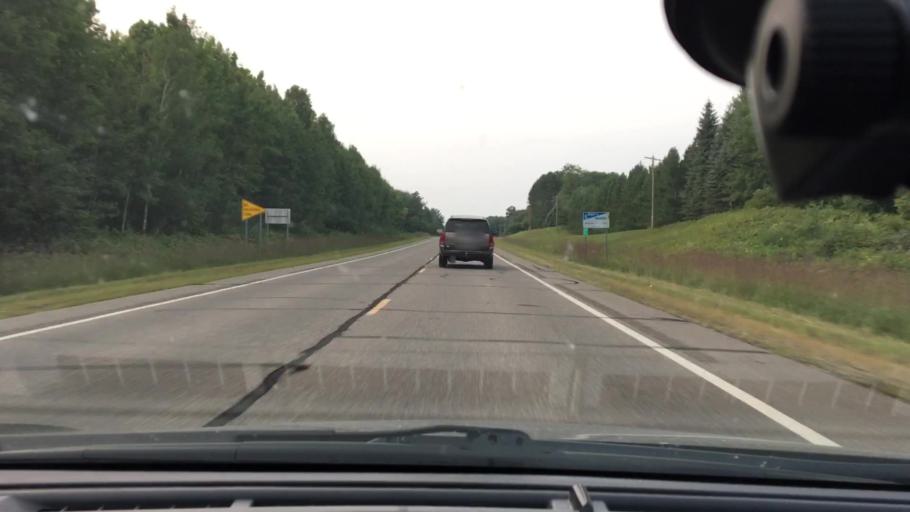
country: US
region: Minnesota
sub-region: Crow Wing County
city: Crosby
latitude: 46.4274
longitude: -93.8734
